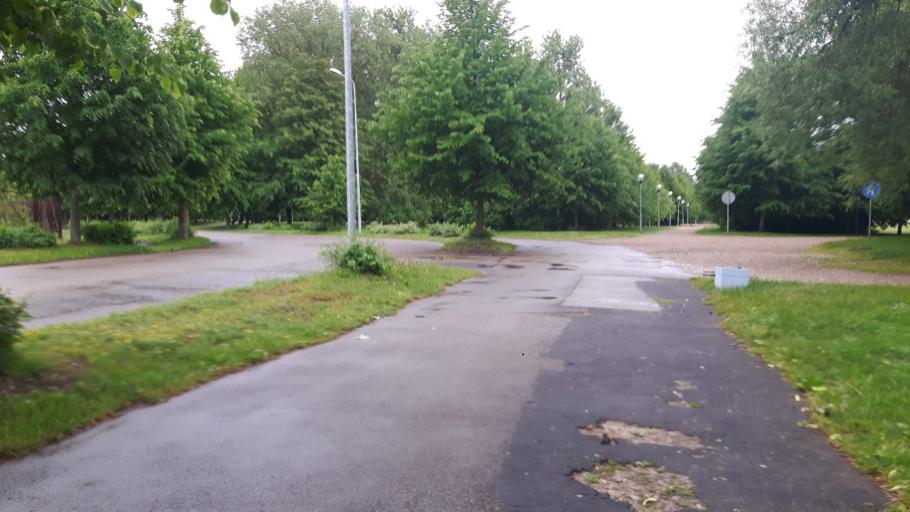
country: LV
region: Liepaja
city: Liepaja
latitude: 56.5109
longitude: 20.9926
